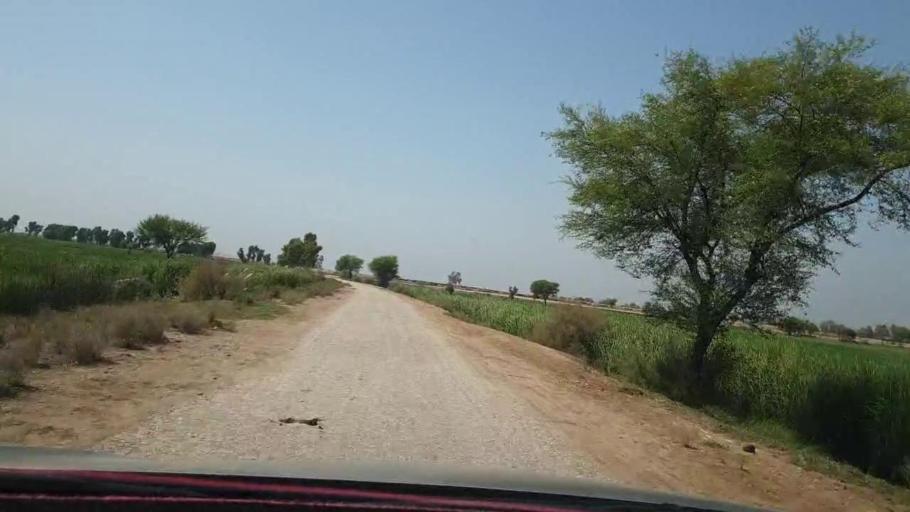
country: PK
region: Sindh
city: Warah
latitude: 27.5484
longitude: 67.7399
